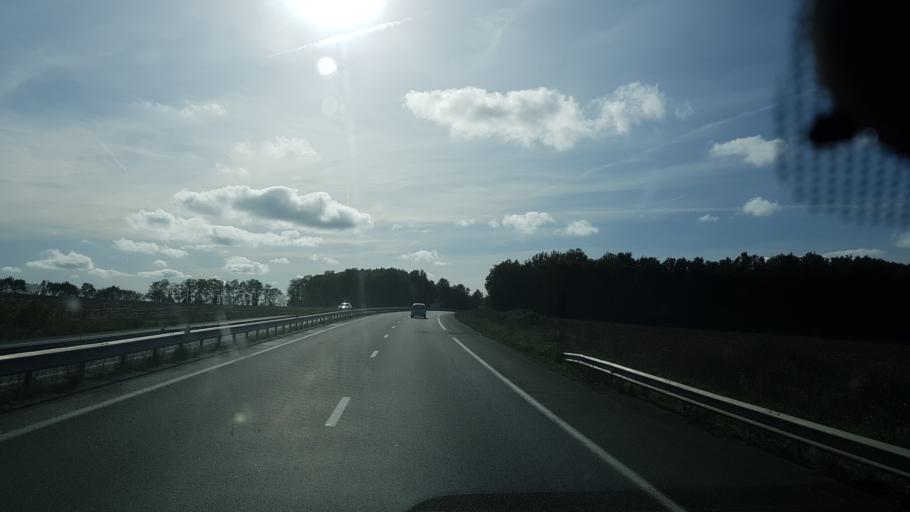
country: FR
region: Poitou-Charentes
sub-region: Departement de la Charente
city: Chasseneuil-sur-Bonnieure
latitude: 45.7965
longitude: 0.4335
